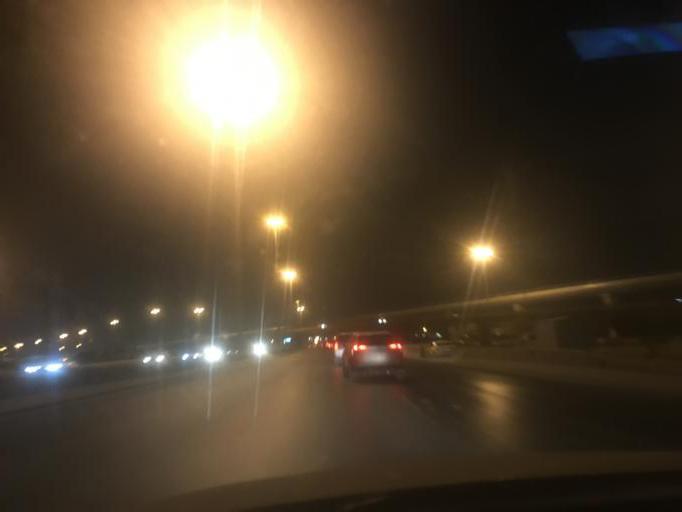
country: SA
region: Ar Riyad
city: Riyadh
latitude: 24.8270
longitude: 46.7212
